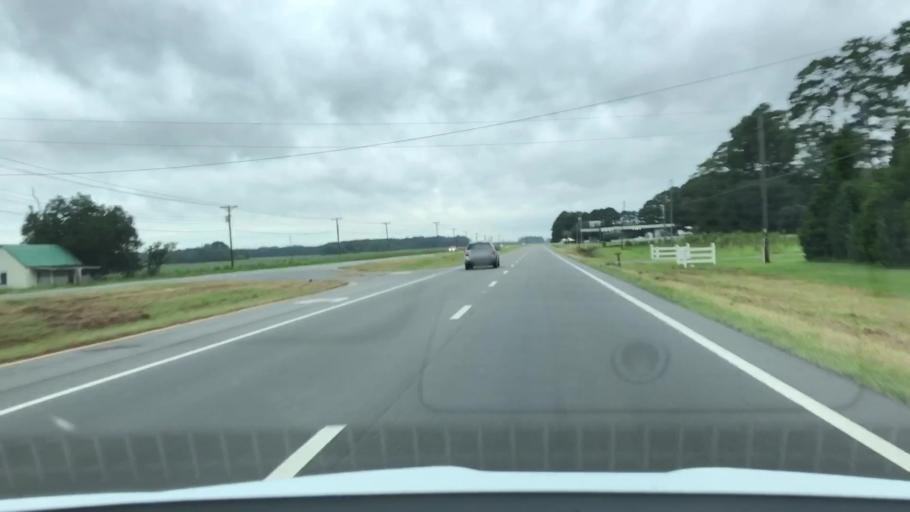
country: US
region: North Carolina
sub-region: Lenoir County
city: La Grange
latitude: 35.2600
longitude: -77.7040
